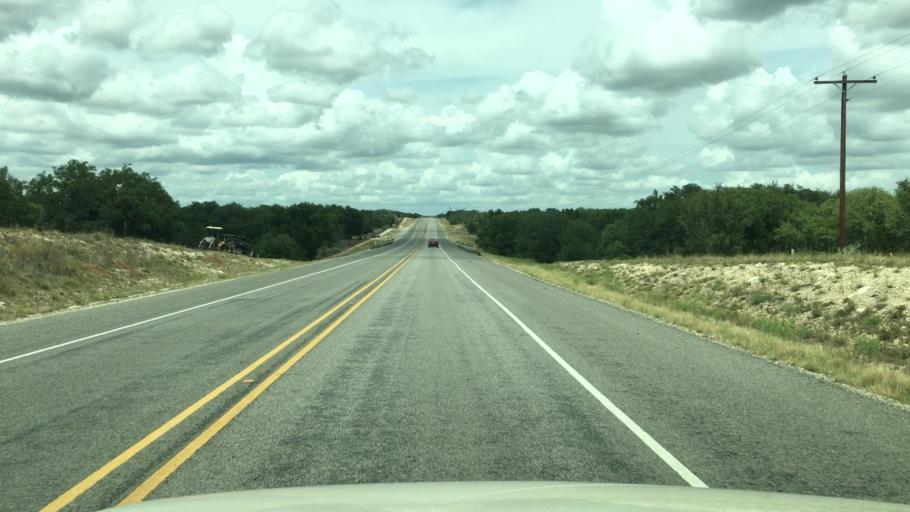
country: US
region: Texas
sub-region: McCulloch County
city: Brady
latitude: 31.0392
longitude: -99.2403
